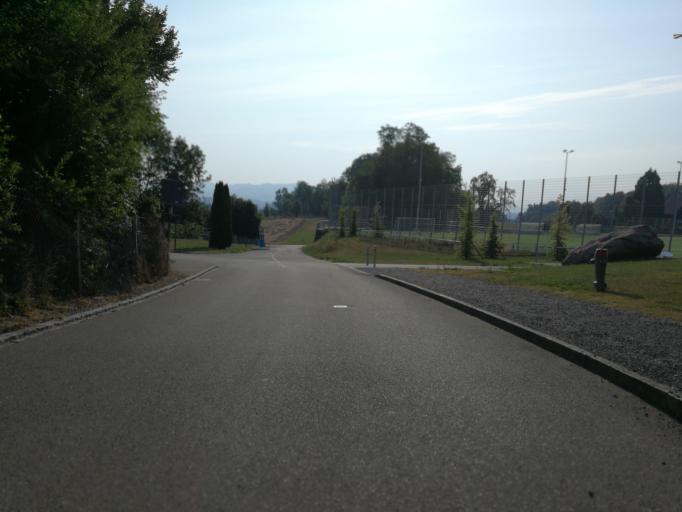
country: CH
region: Zurich
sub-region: Bezirk Uster
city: Egg
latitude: 47.3001
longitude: 8.6943
